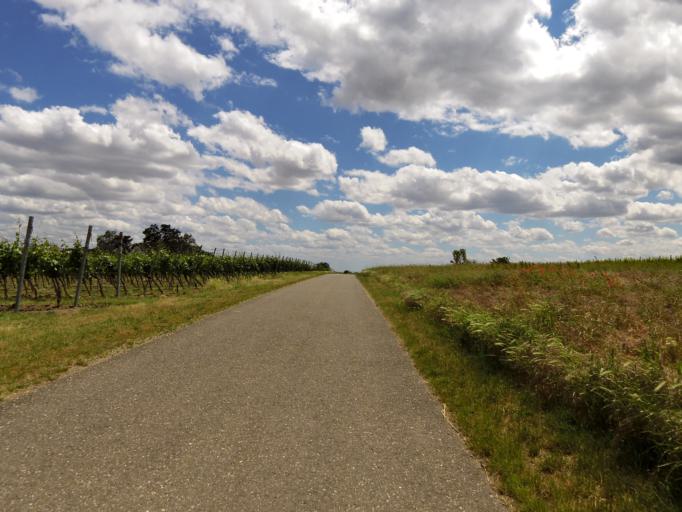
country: DE
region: Rheinland-Pfalz
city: Freinsheim
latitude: 49.5008
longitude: 8.1991
